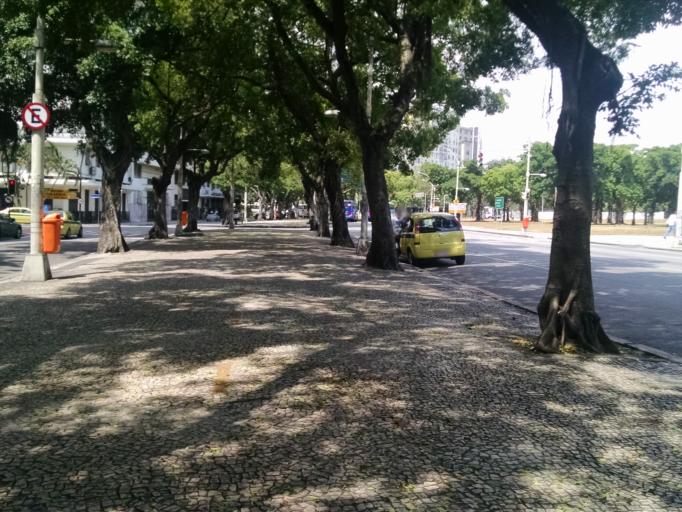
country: BR
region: Rio de Janeiro
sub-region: Rio De Janeiro
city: Rio de Janeiro
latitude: -22.9127
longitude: -43.1750
